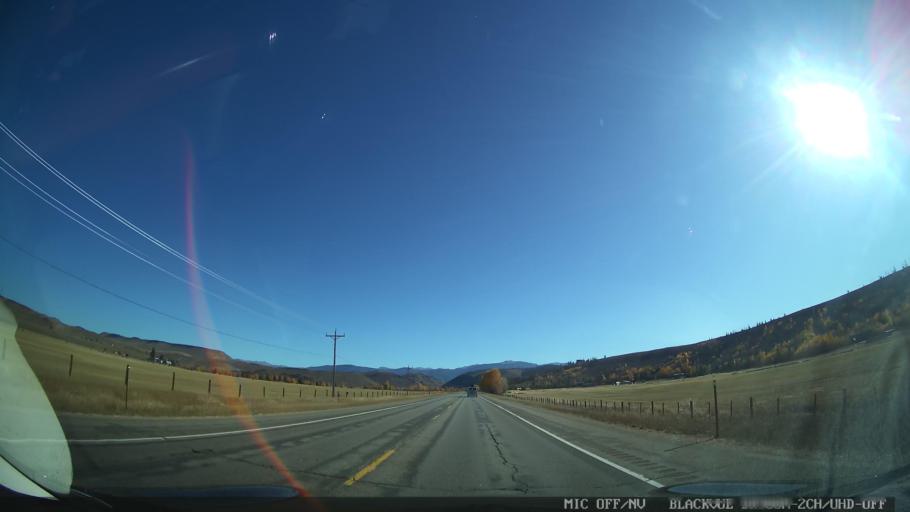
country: US
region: Colorado
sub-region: Grand County
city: Granby
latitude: 40.1130
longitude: -105.9204
